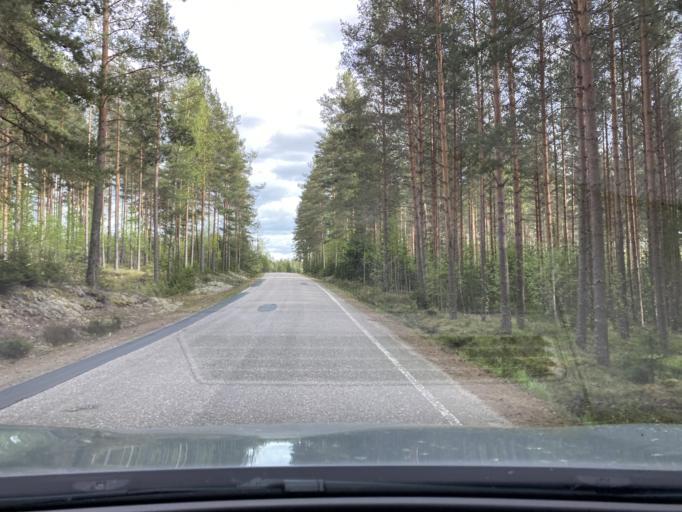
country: FI
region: Varsinais-Suomi
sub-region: Salo
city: Kiikala
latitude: 60.4995
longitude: 23.5510
